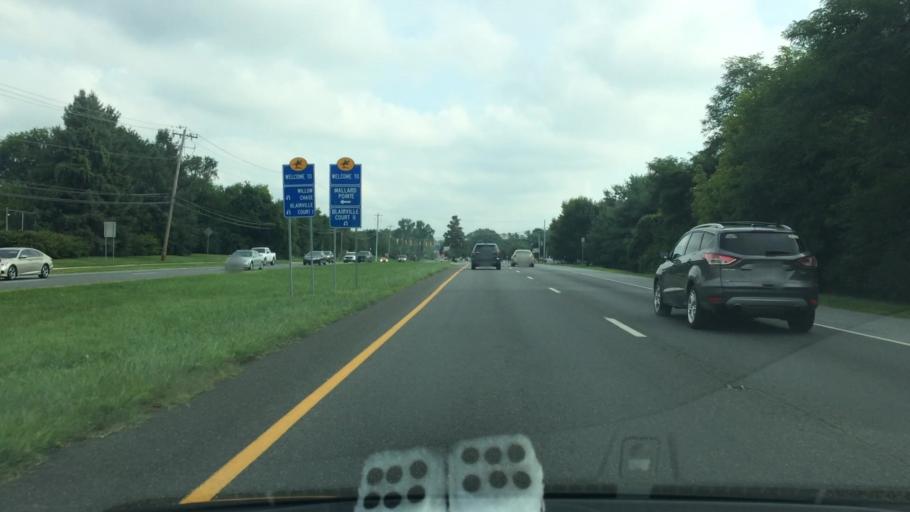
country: US
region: Delaware
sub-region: New Castle County
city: Bear
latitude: 39.6393
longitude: -75.6282
